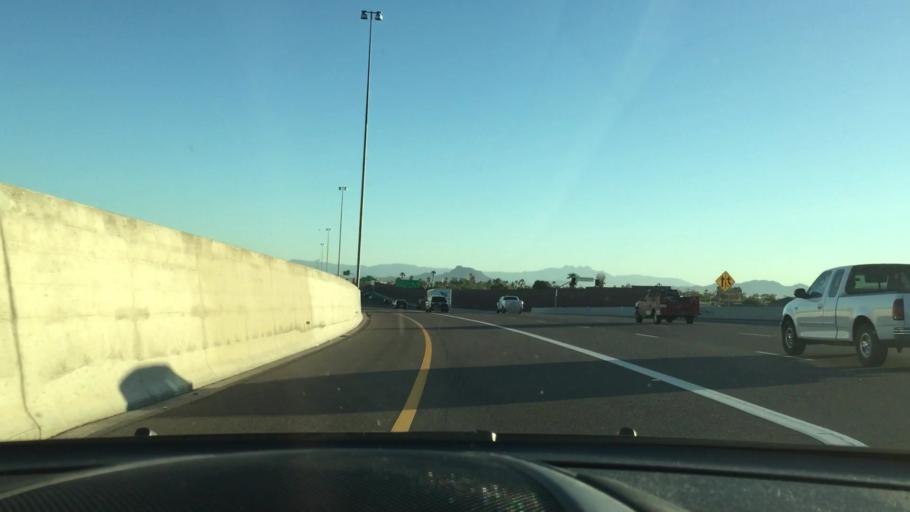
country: US
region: Arizona
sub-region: Maricopa County
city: Mesa
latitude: 33.4465
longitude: -111.8525
